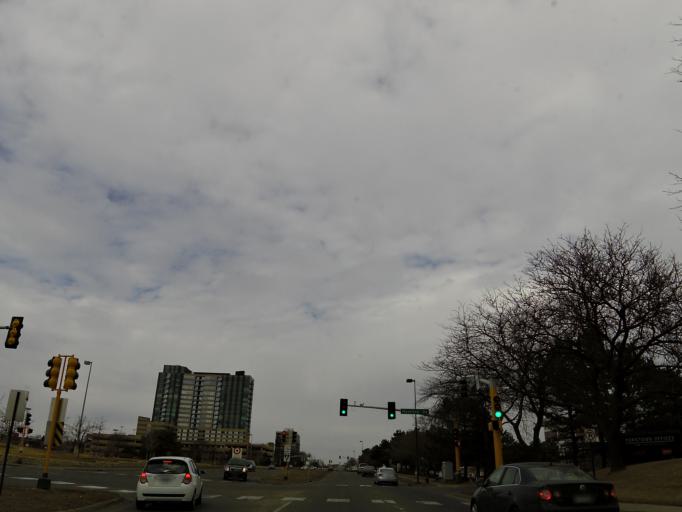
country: US
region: Minnesota
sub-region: Hennepin County
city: Edina
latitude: 44.8741
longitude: -93.3211
